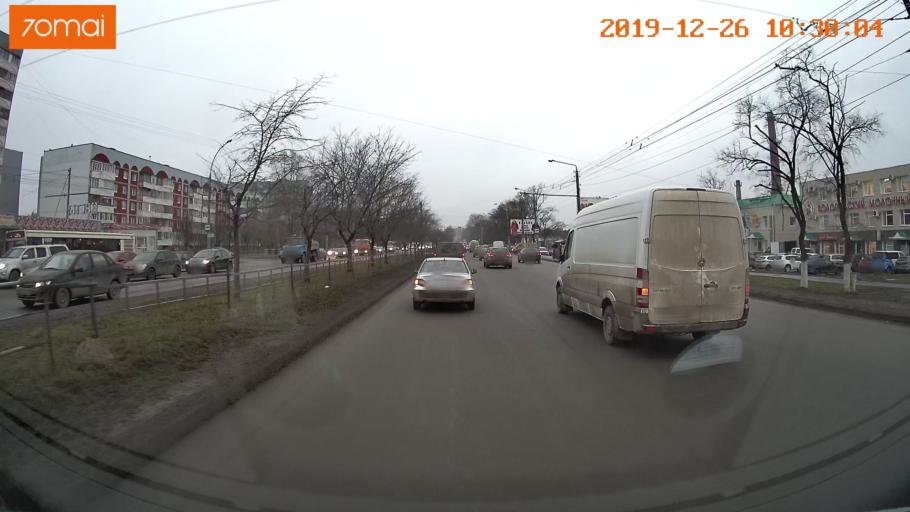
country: RU
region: Vologda
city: Vologda
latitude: 59.2028
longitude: 39.8682
